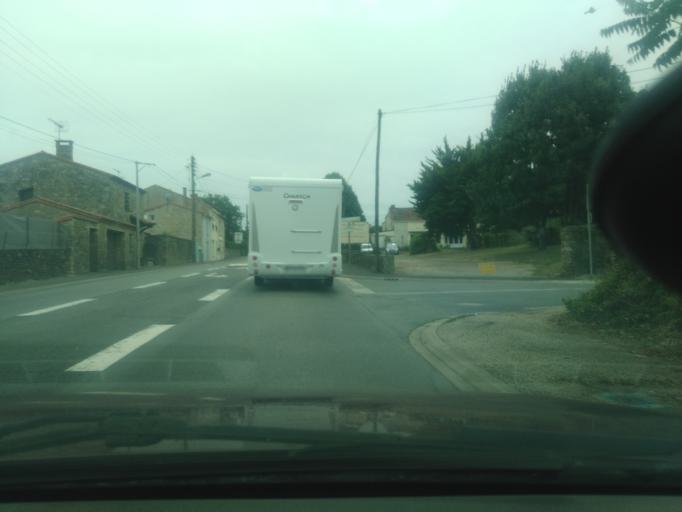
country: FR
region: Pays de la Loire
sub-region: Departement de la Vendee
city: Sainte-Cecile
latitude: 46.7432
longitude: -1.0885
